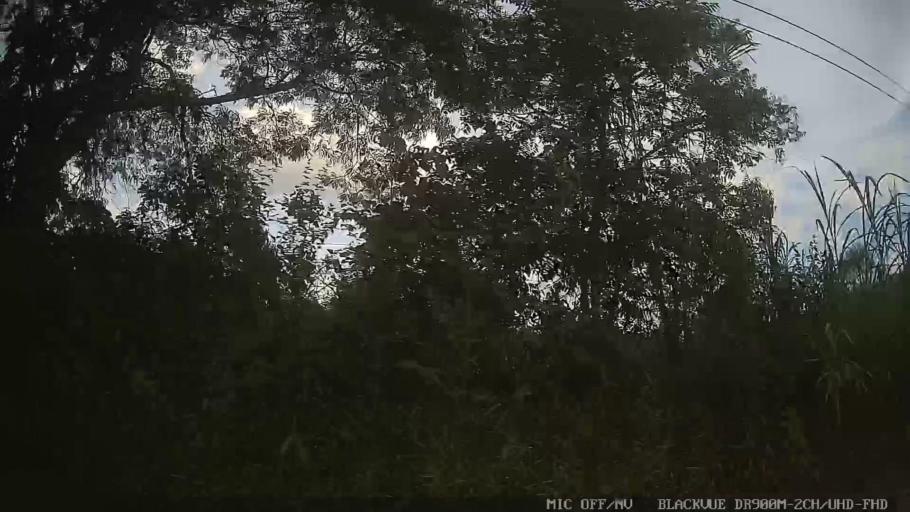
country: BR
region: Sao Paulo
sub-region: Bom Jesus Dos Perdoes
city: Bom Jesus dos Perdoes
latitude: -23.1299
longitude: -46.5014
